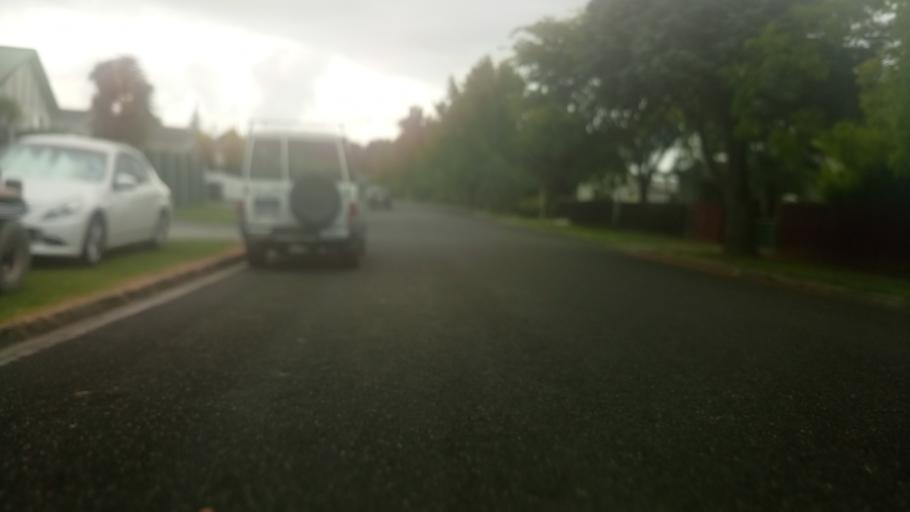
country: NZ
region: Gisborne
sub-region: Gisborne District
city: Gisborne
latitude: -38.6459
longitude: 177.9884
